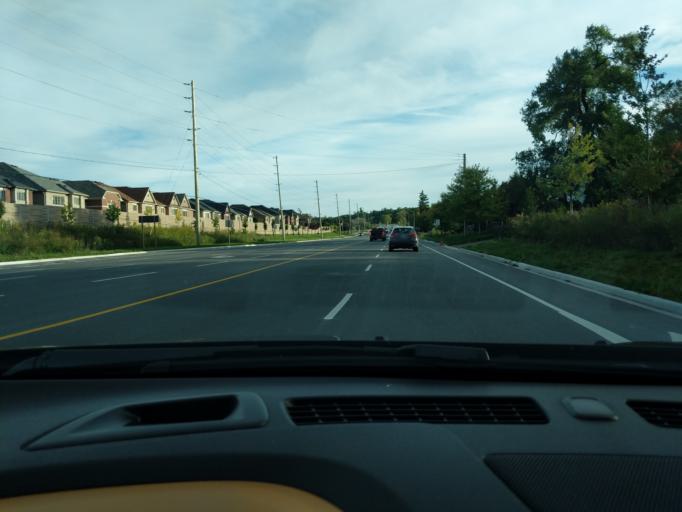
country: CA
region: Ontario
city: Newmarket
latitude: 44.0480
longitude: -79.5061
